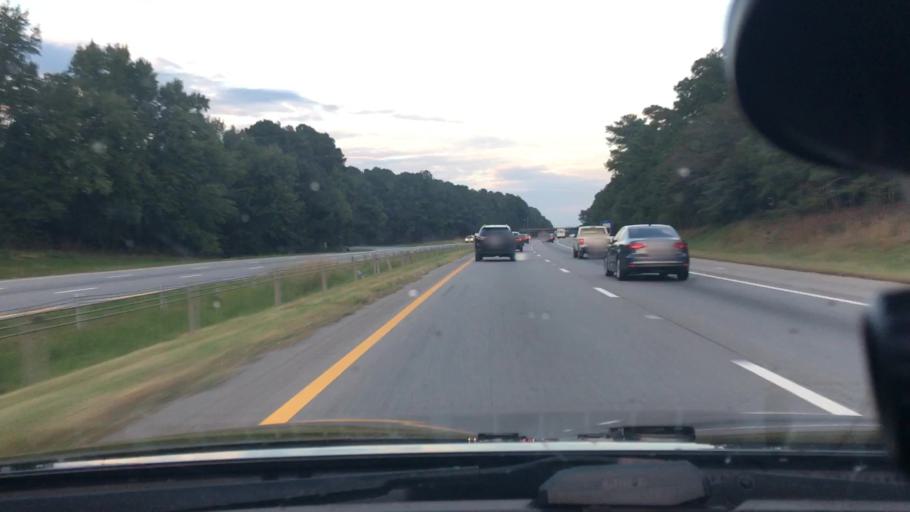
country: US
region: North Carolina
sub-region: Wake County
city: Apex
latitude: 35.7219
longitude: -78.8291
